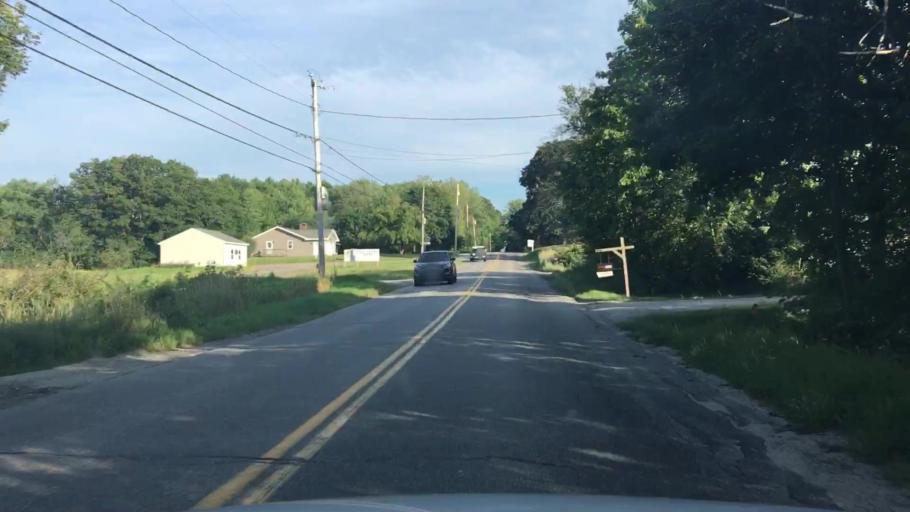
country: US
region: Maine
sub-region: Cumberland County
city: South Windham
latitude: 43.7194
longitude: -70.3967
